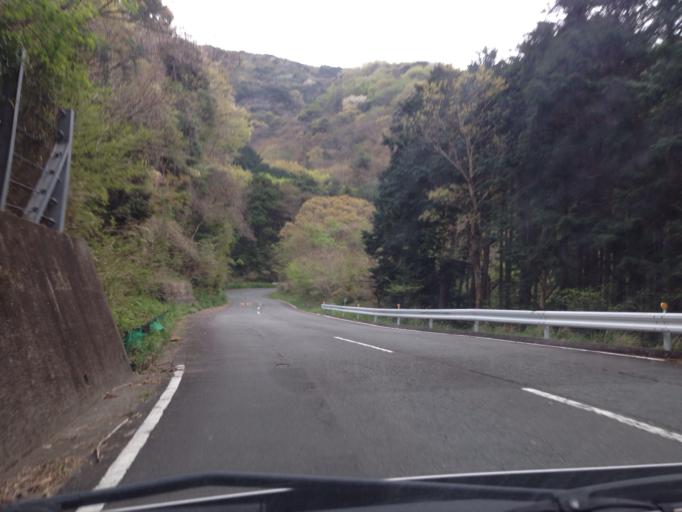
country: JP
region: Shizuoka
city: Heda
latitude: 34.9938
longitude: 138.7800
